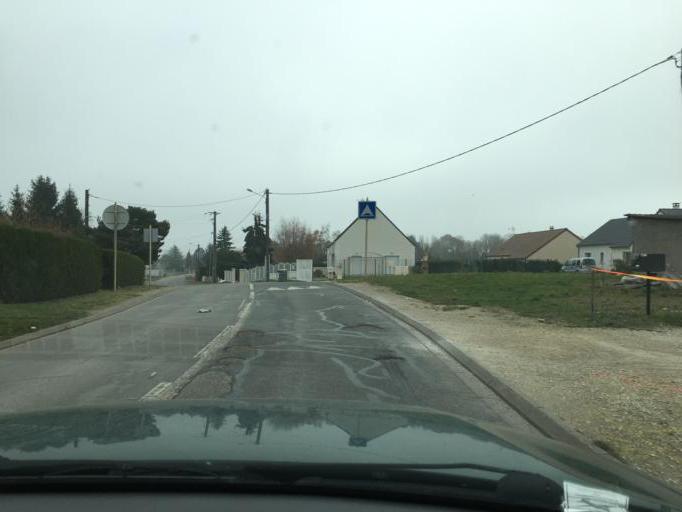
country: FR
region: Centre
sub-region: Departement du Loiret
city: Ormes
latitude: 47.9545
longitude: 1.8272
